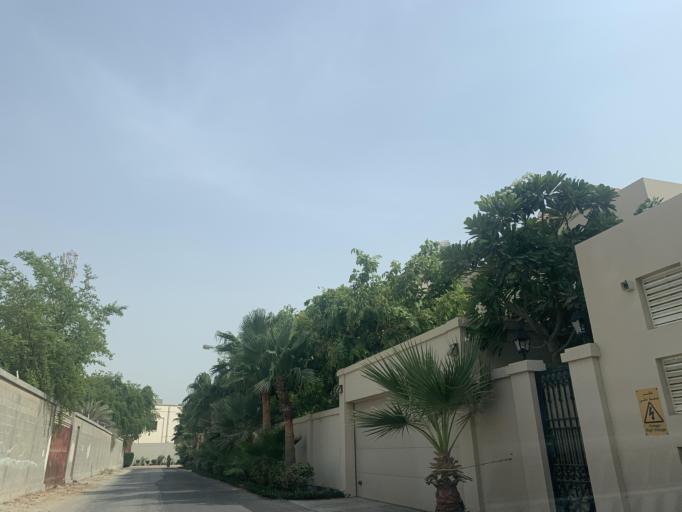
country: BH
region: Manama
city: Jidd Hafs
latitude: 26.1995
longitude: 50.4804
